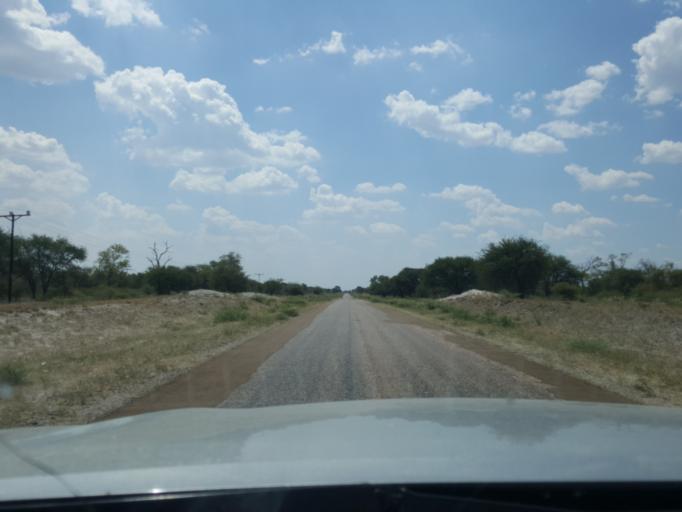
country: BW
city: Tsau
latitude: -19.9742
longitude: 22.2530
